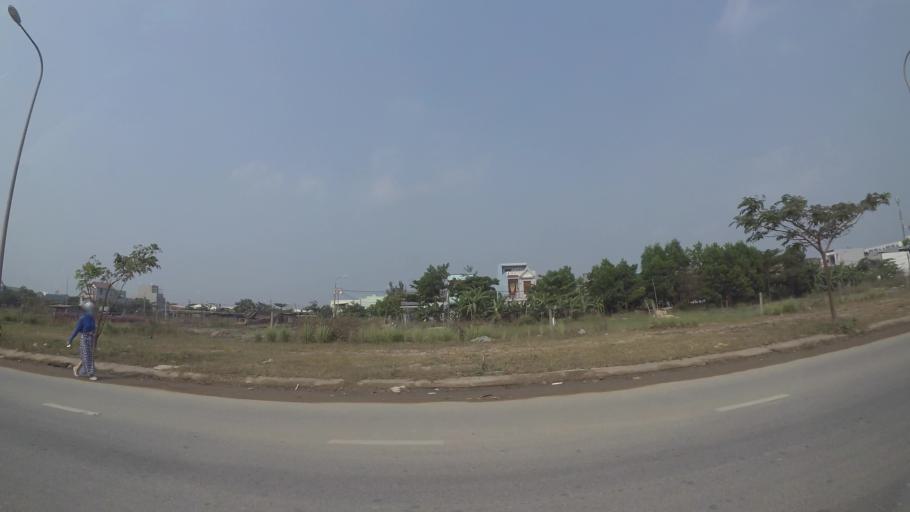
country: VN
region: Da Nang
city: Cam Le
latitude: 15.9958
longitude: 108.2162
